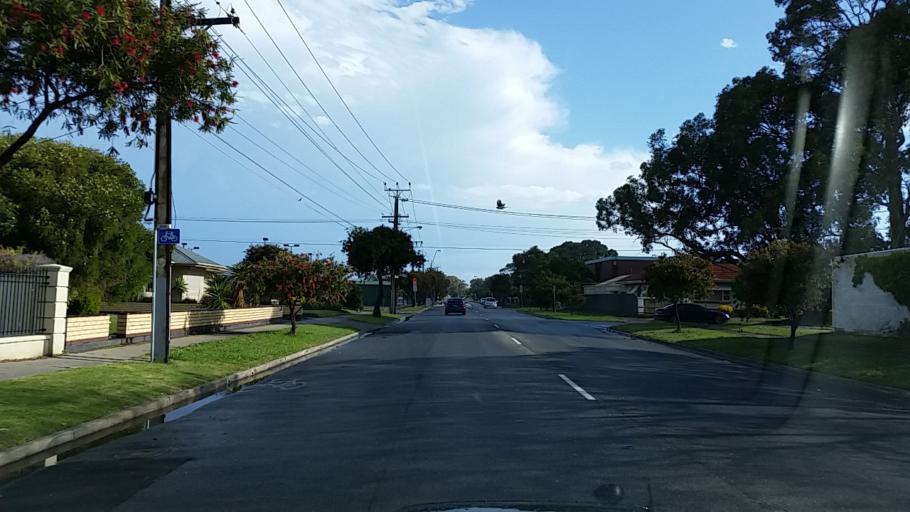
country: AU
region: South Australia
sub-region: Charles Sturt
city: Henley Beach
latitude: -34.9208
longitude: 138.5014
